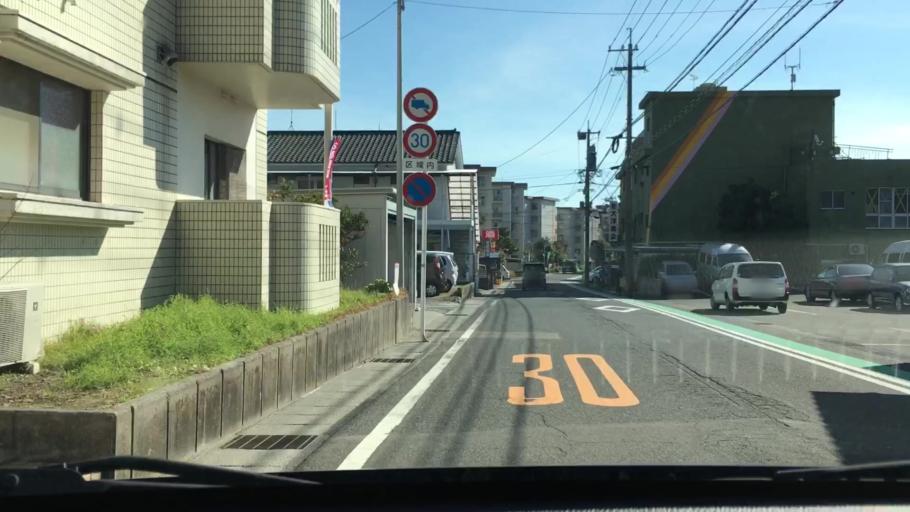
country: JP
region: Kagoshima
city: Kagoshima-shi
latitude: 31.5631
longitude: 130.5314
